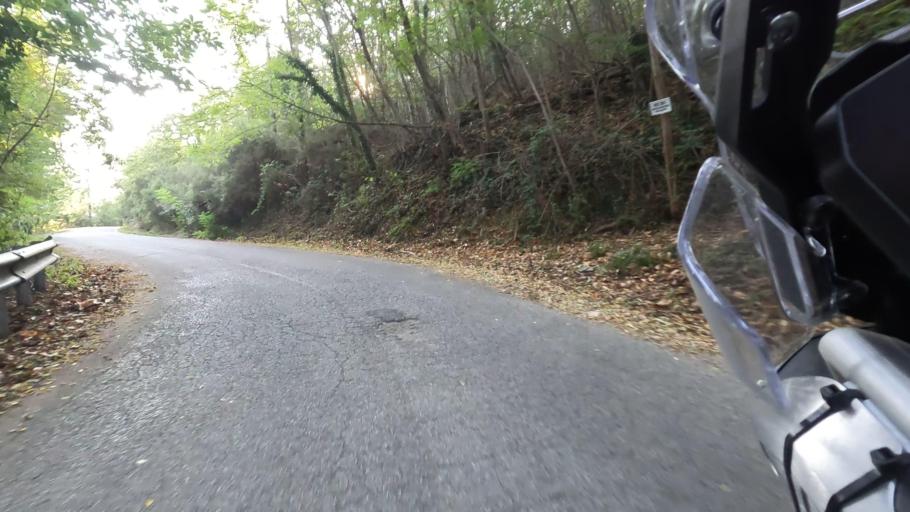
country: IT
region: Liguria
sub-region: Provincia di Savona
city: San Giovanni
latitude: 44.3932
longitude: 8.5356
